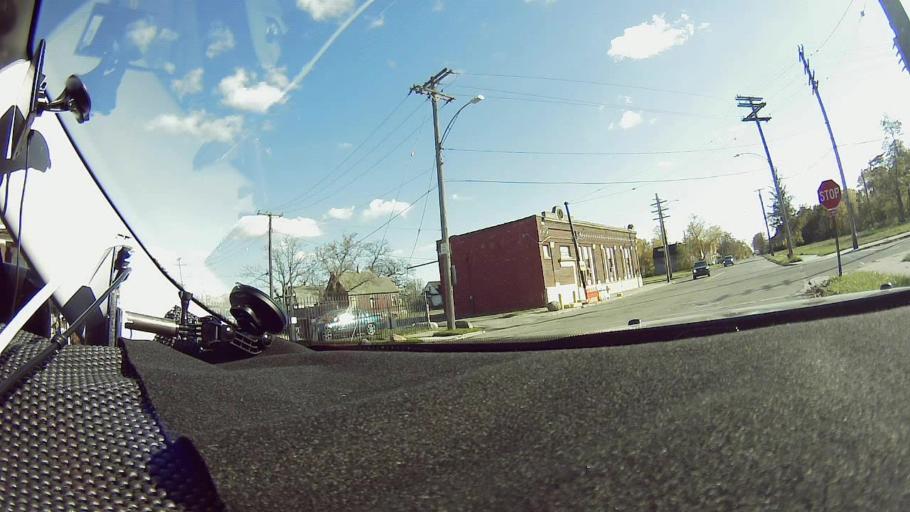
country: US
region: Michigan
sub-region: Wayne County
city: Detroit
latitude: 42.3385
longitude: -83.1066
